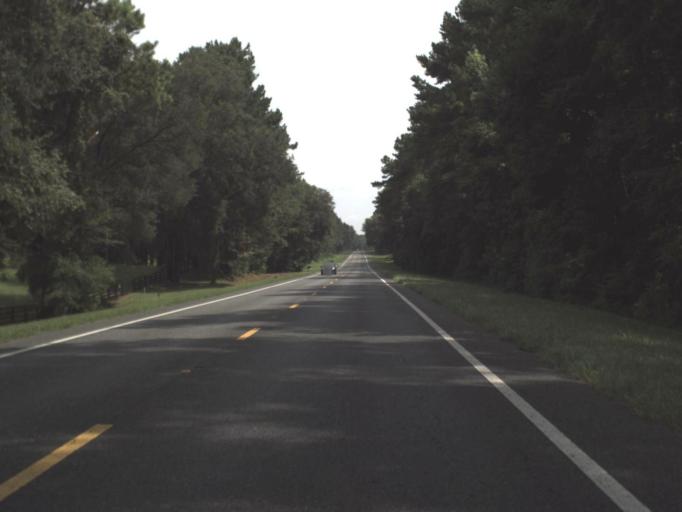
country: US
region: Florida
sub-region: Alachua County
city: High Springs
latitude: 29.9218
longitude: -82.6093
